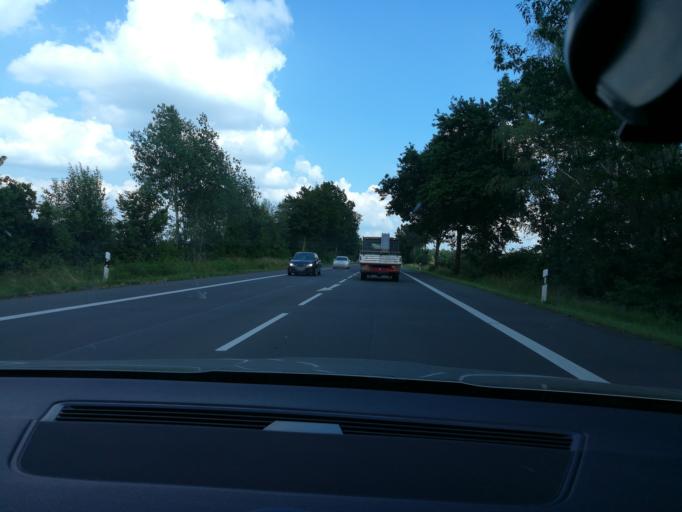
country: DE
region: North Rhine-Westphalia
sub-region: Regierungsbezirk Detmold
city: Petershagen
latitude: 52.3806
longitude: 8.9168
